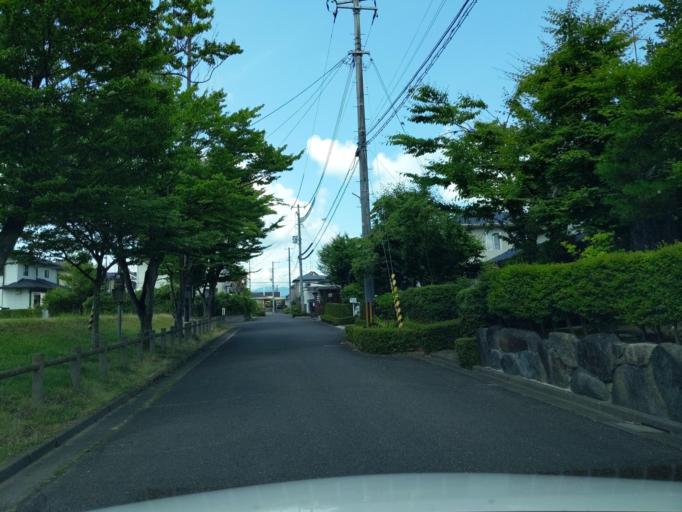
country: JP
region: Fukushima
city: Sukagawa
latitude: 37.3415
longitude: 140.3481
